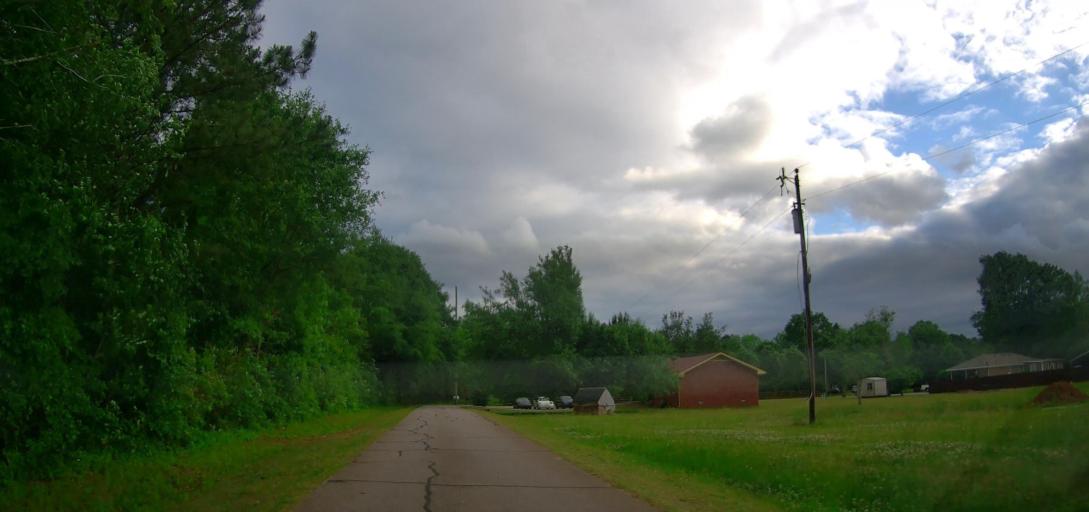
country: US
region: Georgia
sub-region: Oconee County
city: Watkinsville
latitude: 33.8231
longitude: -83.4469
